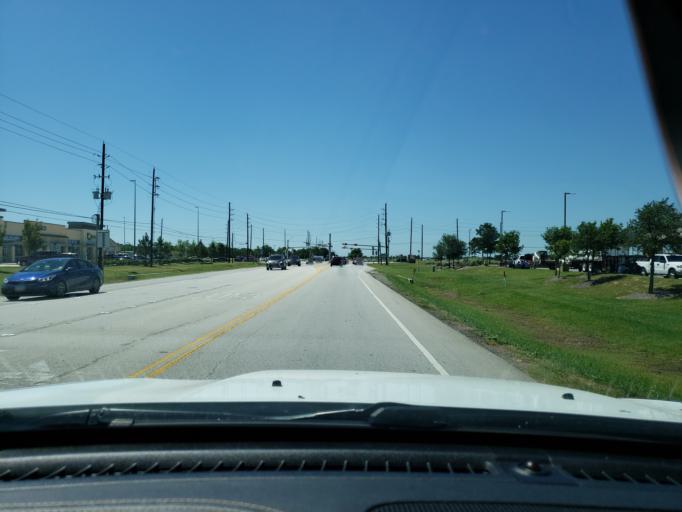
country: US
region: Texas
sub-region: Fort Bend County
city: Fulshear
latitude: 29.6966
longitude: -95.8460
